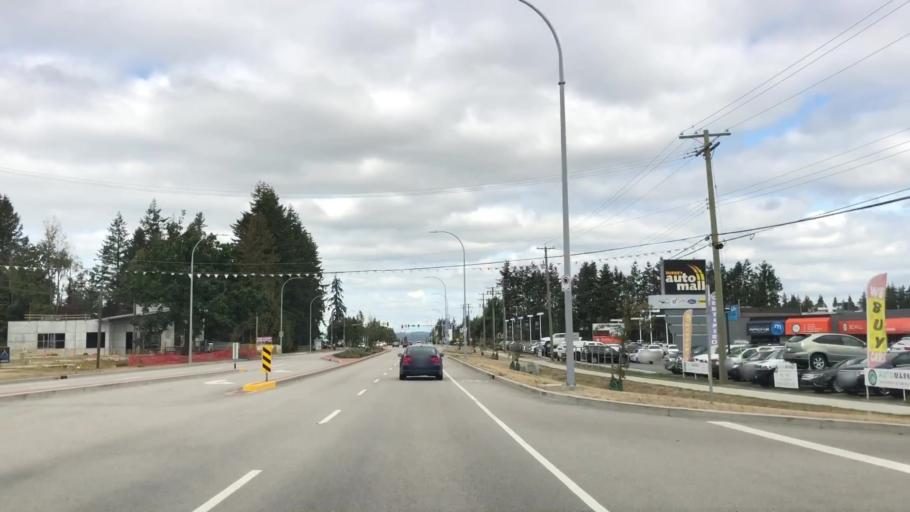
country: CA
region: British Columbia
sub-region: Greater Vancouver Regional District
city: White Rock
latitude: 49.0570
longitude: -122.8075
